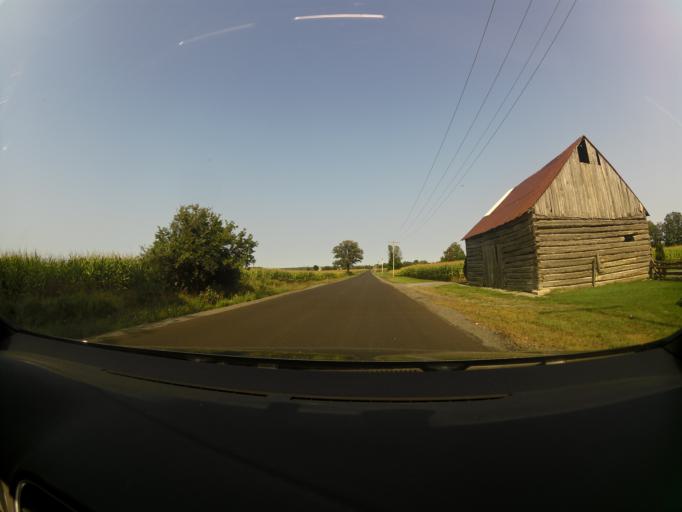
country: CA
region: Ontario
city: Carleton Place
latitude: 45.3256
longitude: -76.0945
